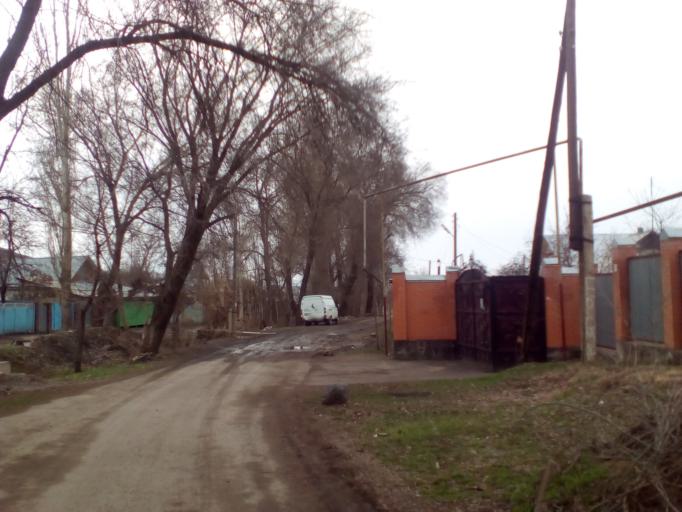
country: KZ
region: Almaty Oblysy
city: Burunday
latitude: 43.1569
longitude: 76.4099
